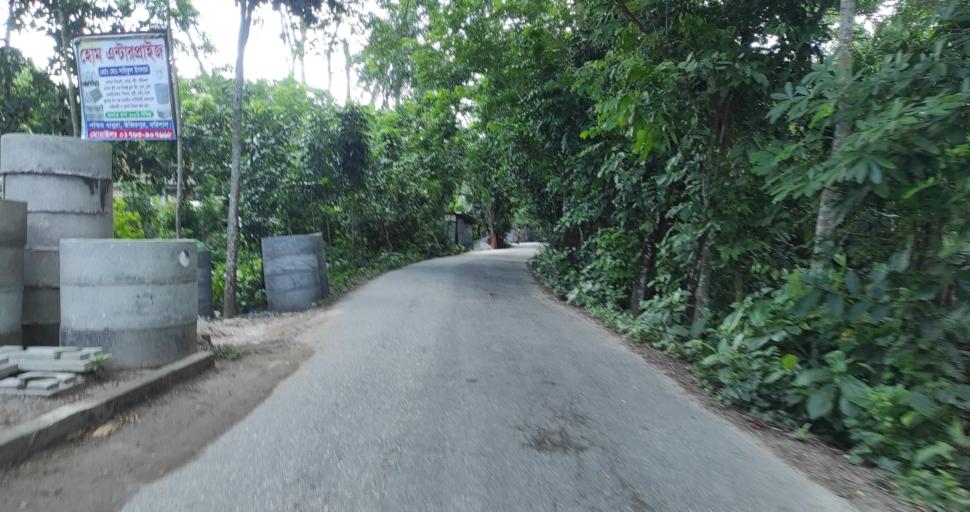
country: BD
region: Barisal
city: Gaurnadi
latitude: 22.8953
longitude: 90.1856
